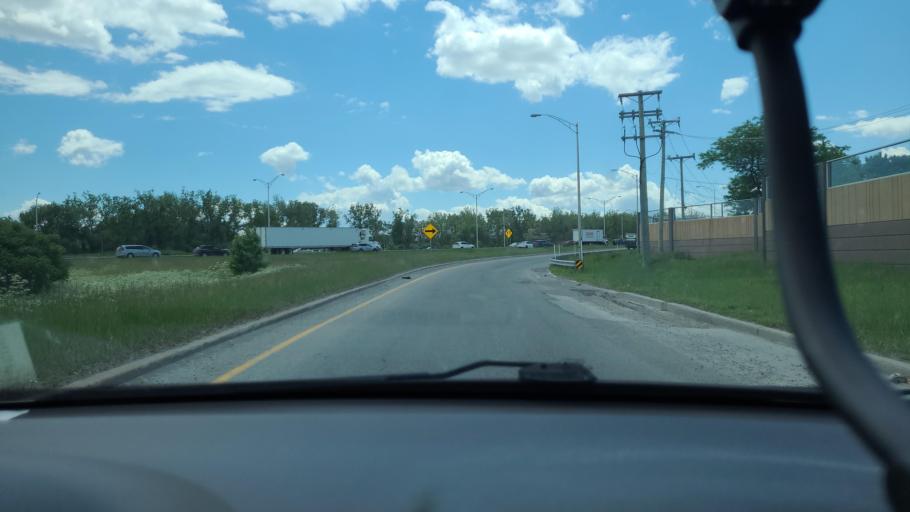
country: CA
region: Quebec
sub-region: Laval
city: Laval
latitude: 45.5926
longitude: -73.7202
